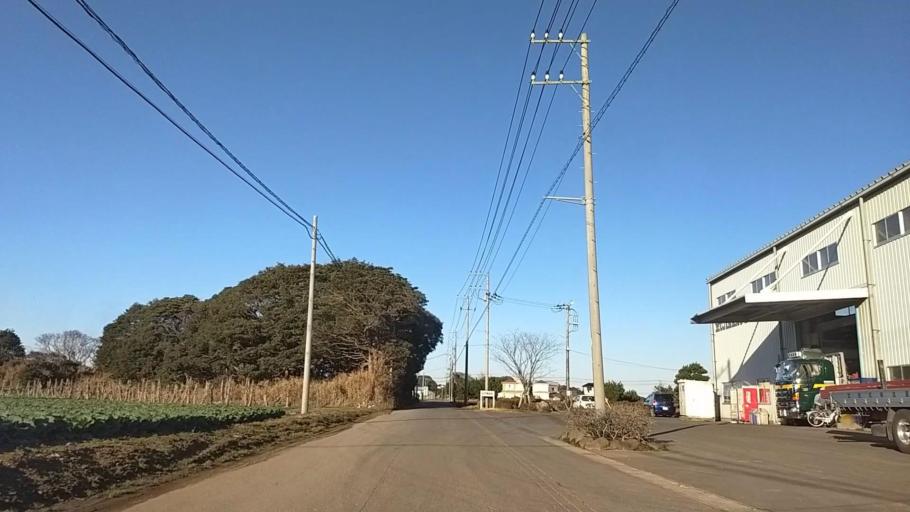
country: JP
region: Chiba
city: Asahi
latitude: 35.7318
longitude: 140.7381
